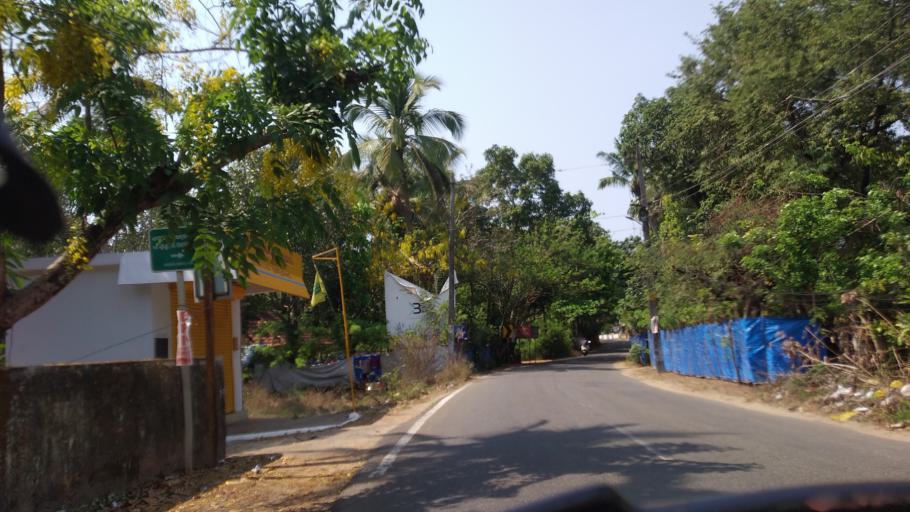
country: IN
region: Kerala
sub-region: Thrissur District
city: Kodungallur
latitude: 10.2303
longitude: 76.1546
